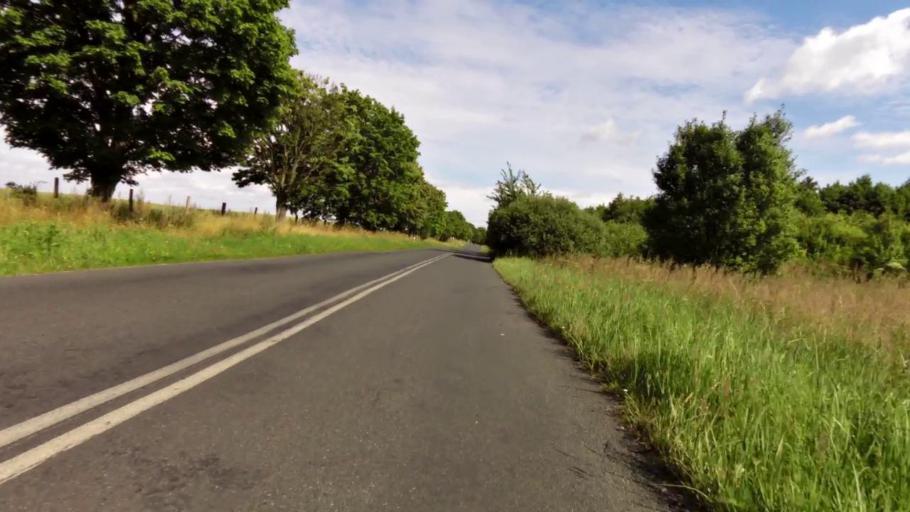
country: PL
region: West Pomeranian Voivodeship
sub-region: Powiat stargardzki
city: Dobrzany
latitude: 53.3941
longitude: 15.4314
